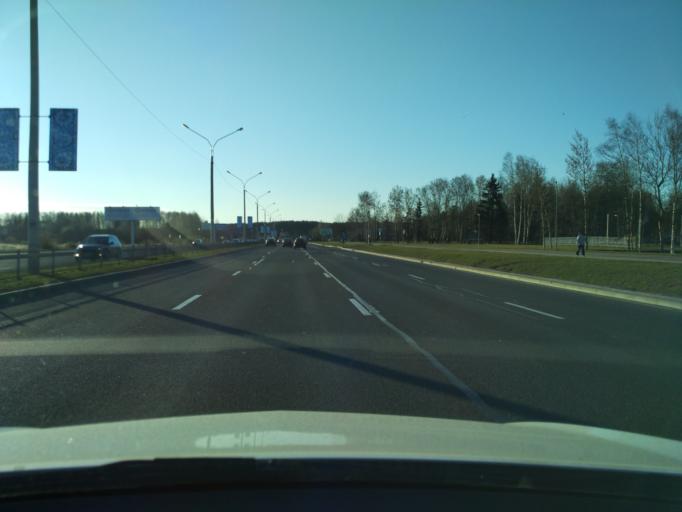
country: BY
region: Minsk
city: Zhdanovichy
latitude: 53.9468
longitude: 27.4561
